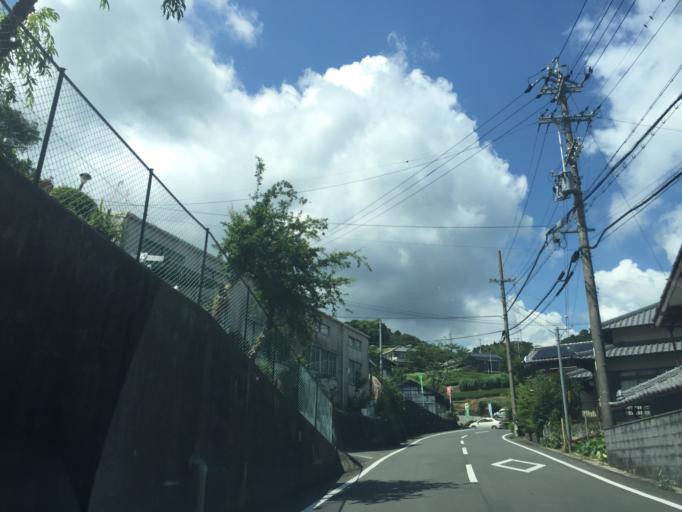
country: JP
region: Shizuoka
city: Kanaya
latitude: 34.8357
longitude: 138.0755
